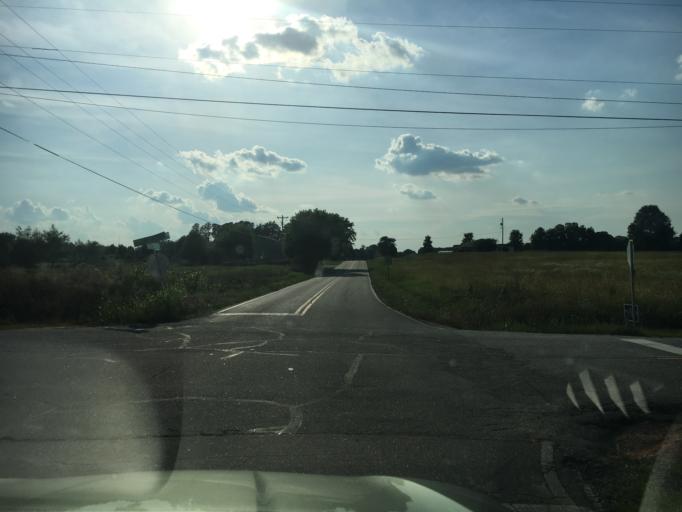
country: US
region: South Carolina
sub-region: Spartanburg County
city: Duncan
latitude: 34.8567
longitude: -82.1187
